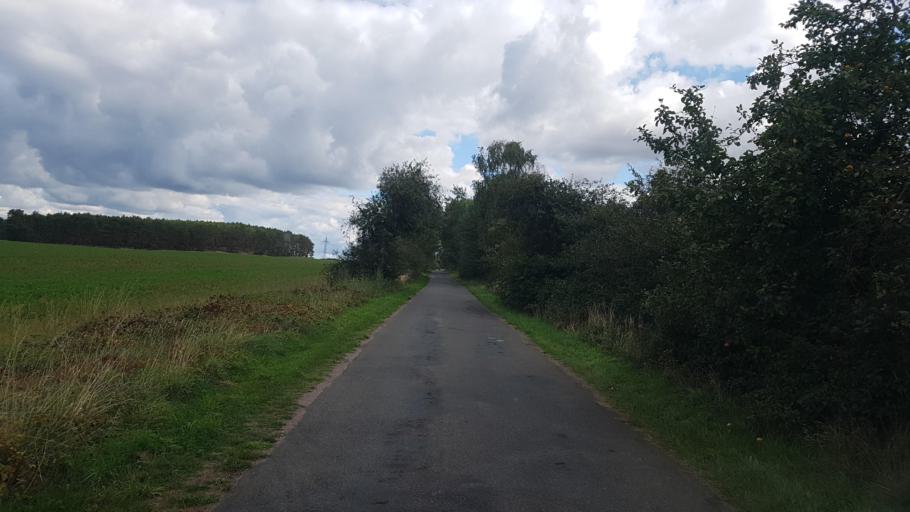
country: DE
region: Brandenburg
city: Linthe
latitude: 52.0695
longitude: 12.7755
